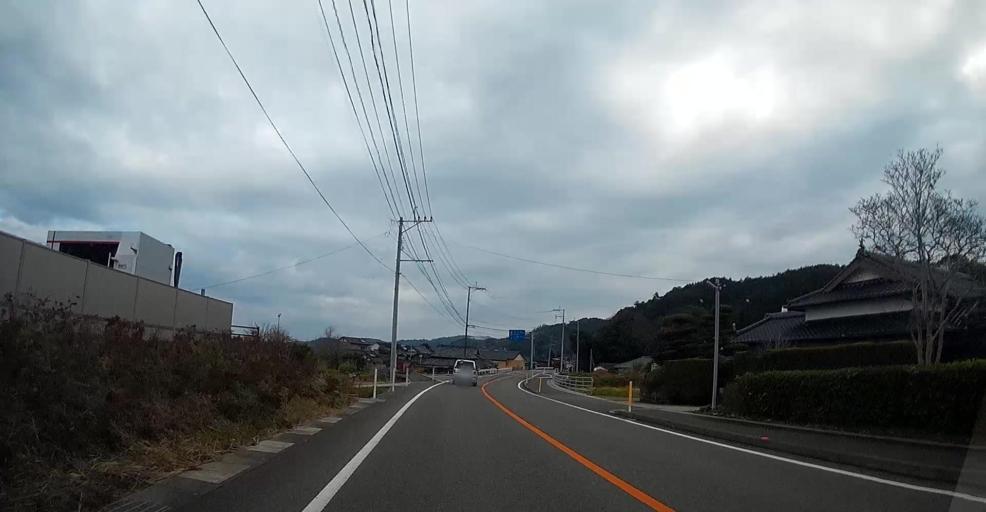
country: JP
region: Kumamoto
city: Hondo
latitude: 32.4832
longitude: 130.2762
